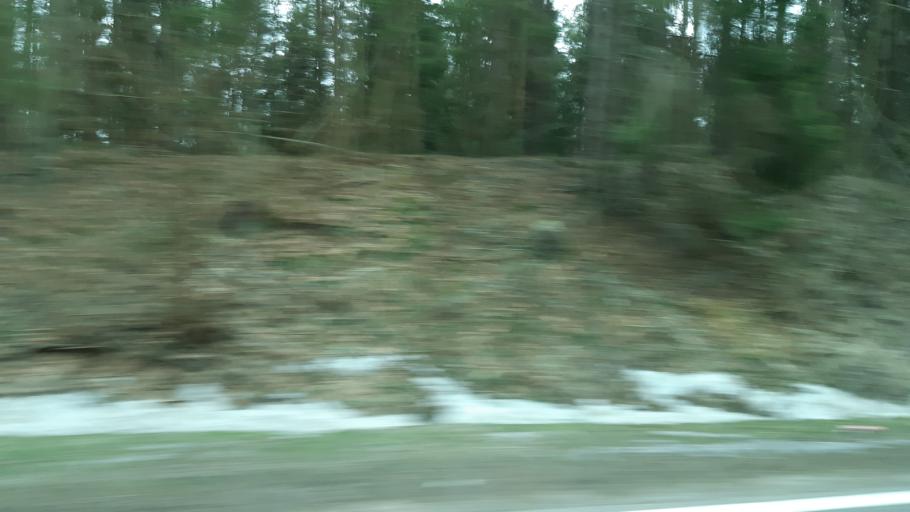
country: PL
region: Podlasie
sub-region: Suwalki
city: Suwalki
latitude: 54.2870
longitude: 22.9534
